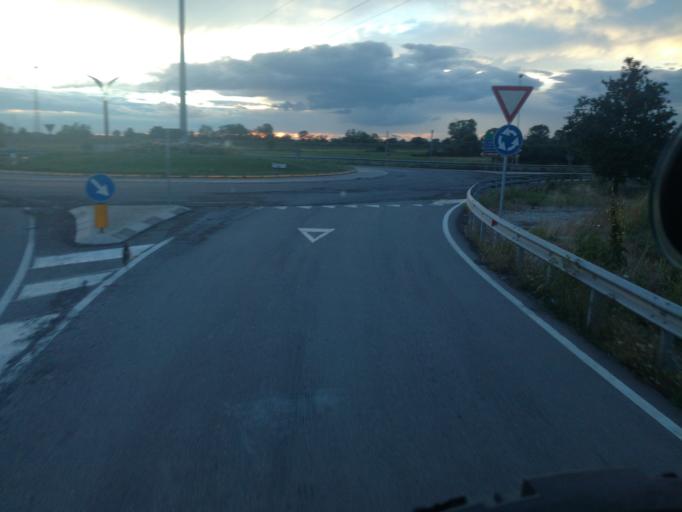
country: IT
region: Emilia-Romagna
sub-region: Provincia di Piacenza
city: Castel San Giovanni
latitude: 45.0806
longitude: 9.4504
